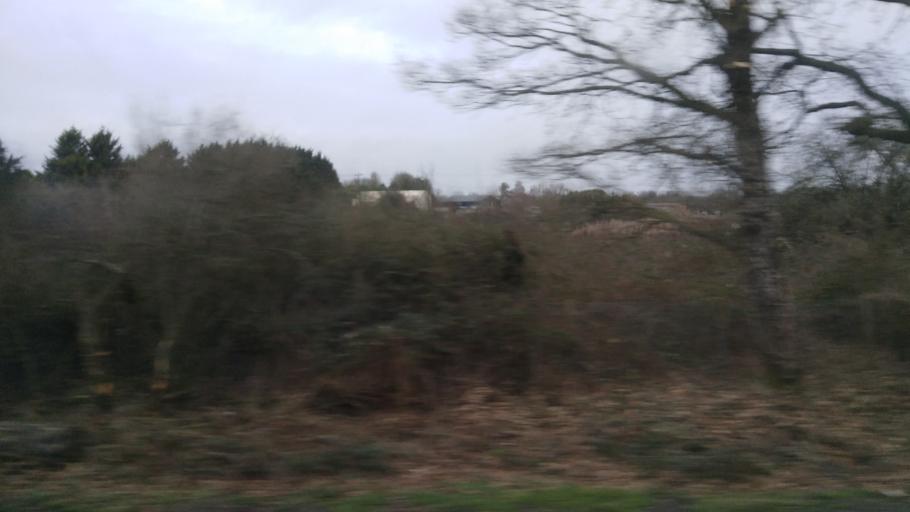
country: GB
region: England
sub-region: Kent
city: Paddock Wood
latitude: 51.1812
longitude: 0.4068
